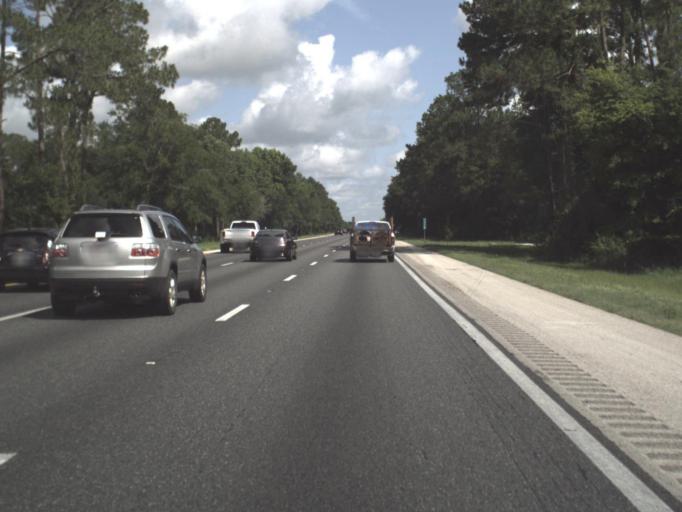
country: US
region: Florida
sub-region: Alachua County
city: Gainesville
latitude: 29.5458
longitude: -82.3341
